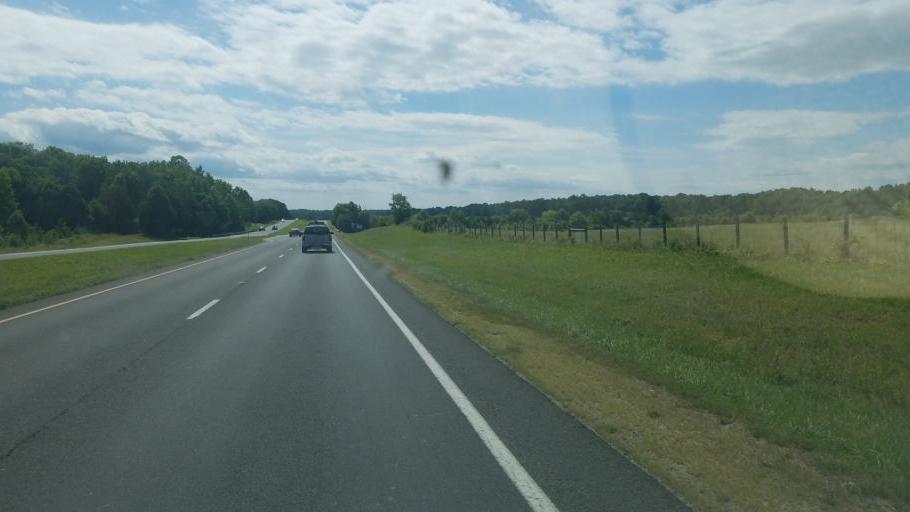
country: US
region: Virginia
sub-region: Fauquier County
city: Bealeton
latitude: 38.4443
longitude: -77.6503
